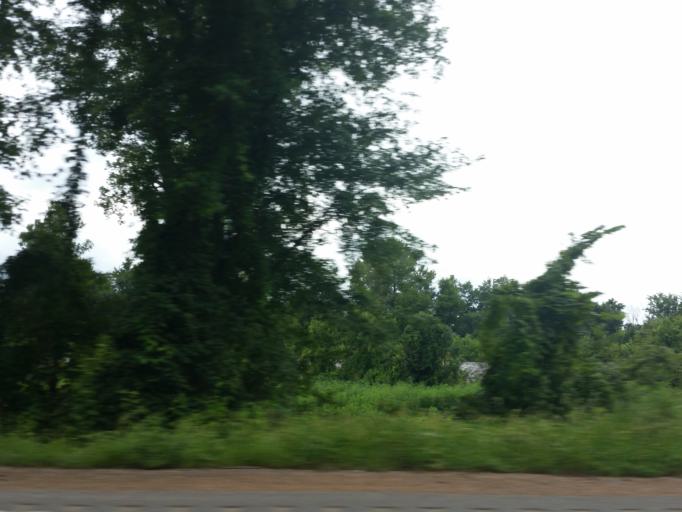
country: US
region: Illinois
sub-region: Alexander County
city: Cairo
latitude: 37.0002
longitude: -89.1365
